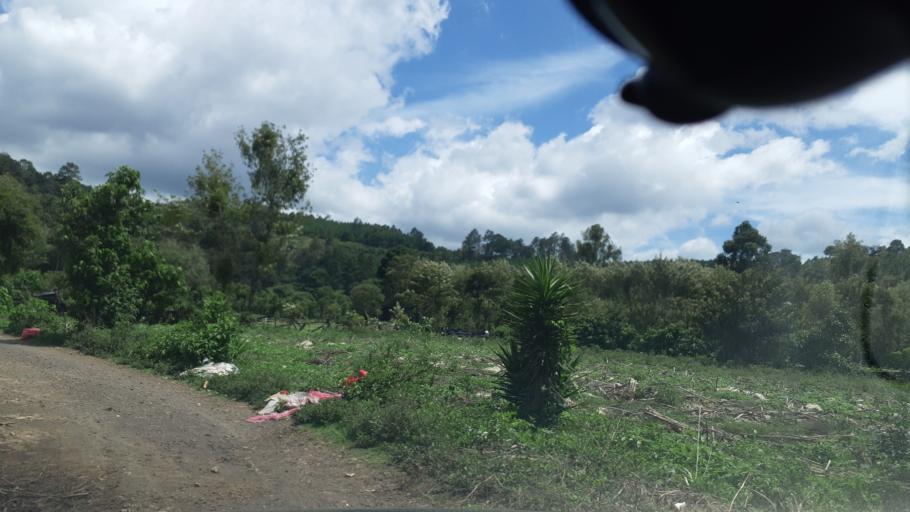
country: GT
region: Chimaltenango
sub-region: Municipio de Chimaltenango
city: Chimaltenango
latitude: 14.6536
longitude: -90.8487
